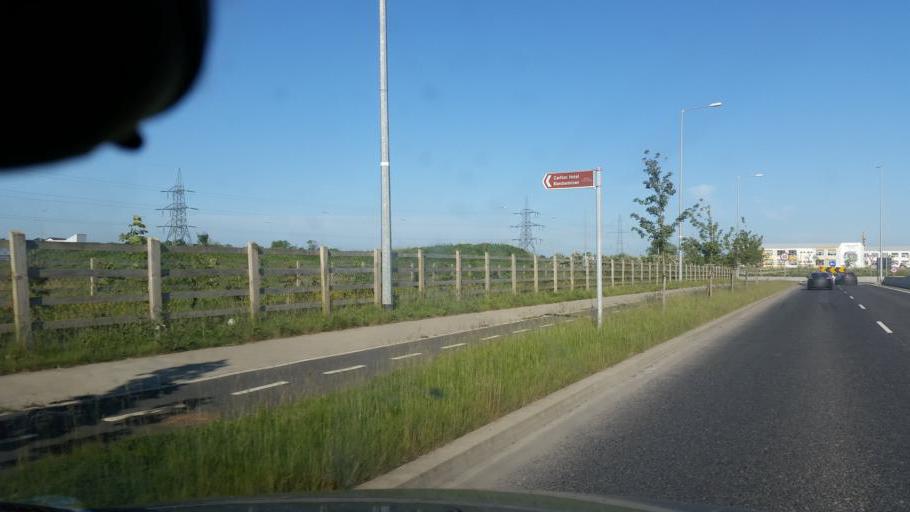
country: IE
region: Leinster
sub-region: Fingal County
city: Blanchardstown
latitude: 53.4221
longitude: -6.3765
